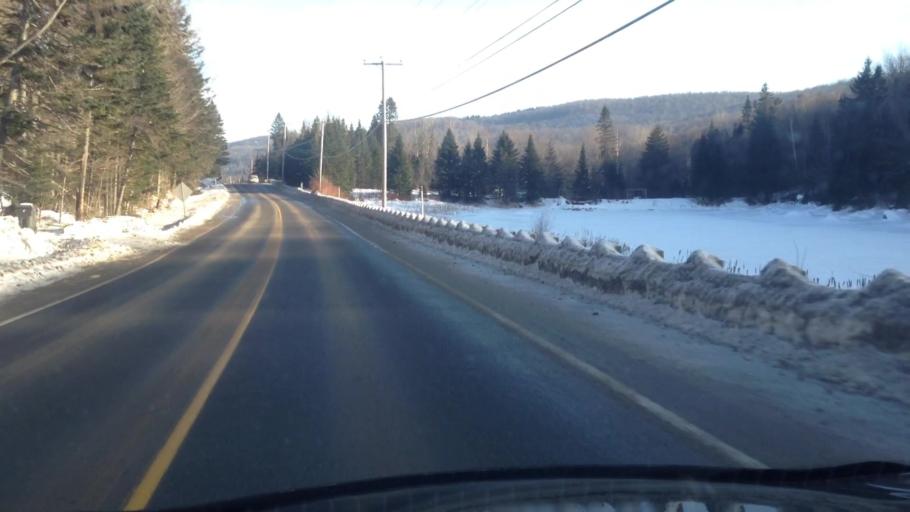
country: CA
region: Quebec
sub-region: Laurentides
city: Saint-Sauveur
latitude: 45.9053
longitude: -74.3211
